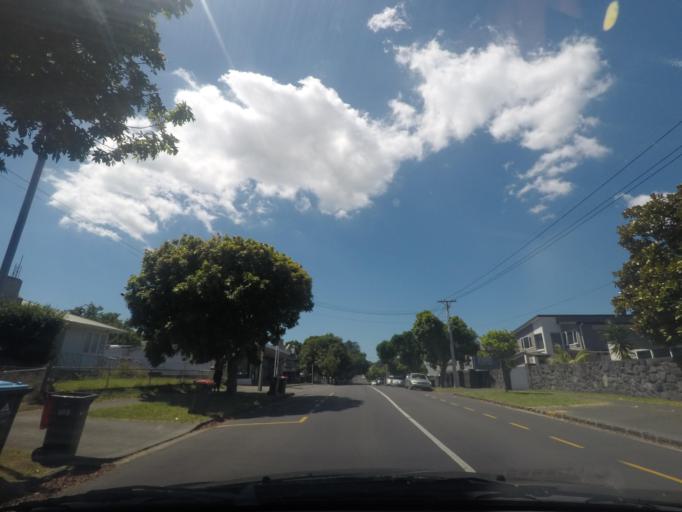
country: NZ
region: Auckland
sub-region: Auckland
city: Auckland
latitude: -36.9069
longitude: 174.7643
